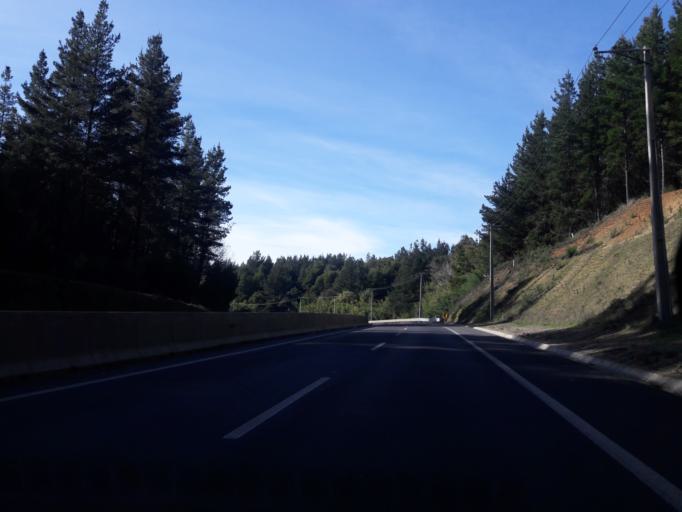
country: CL
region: Biobio
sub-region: Provincia de Concepcion
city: Chiguayante
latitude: -36.8530
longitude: -72.9108
